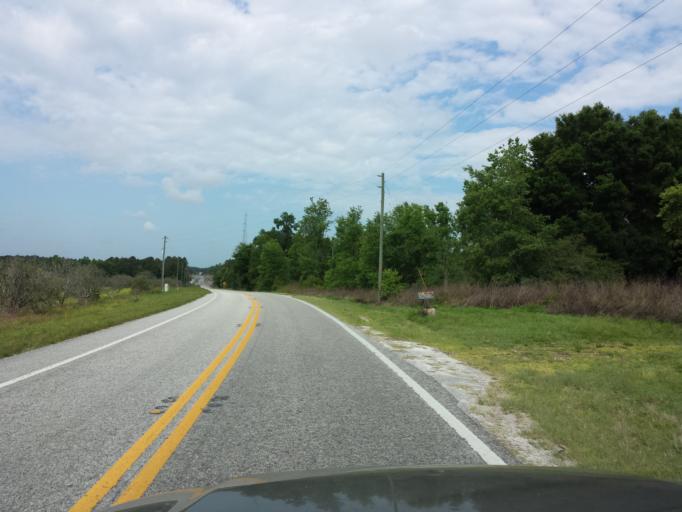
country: US
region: Florida
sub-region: Pasco County
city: San Antonio
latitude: 28.4199
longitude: -82.2798
